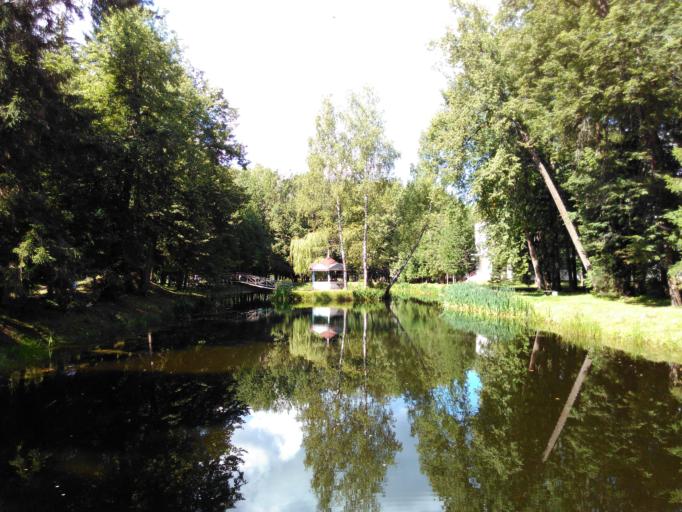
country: RU
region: Tverskaya
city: Konakovo
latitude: 56.6871
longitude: 36.7001
